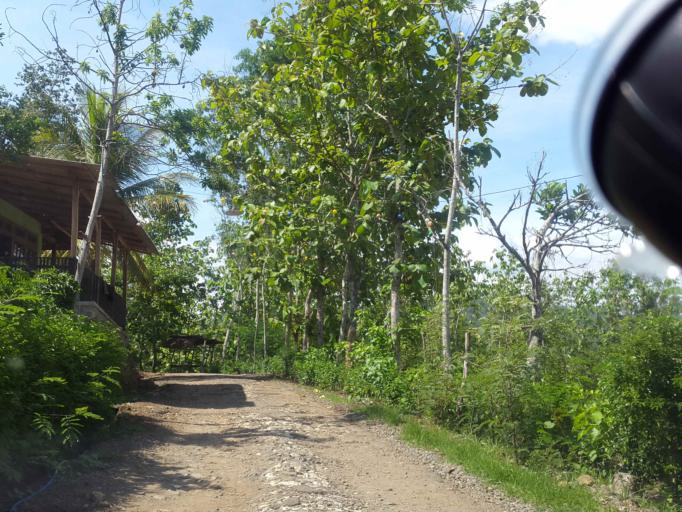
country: ID
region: East Java
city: Ngares
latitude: -8.0179
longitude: 111.6923
